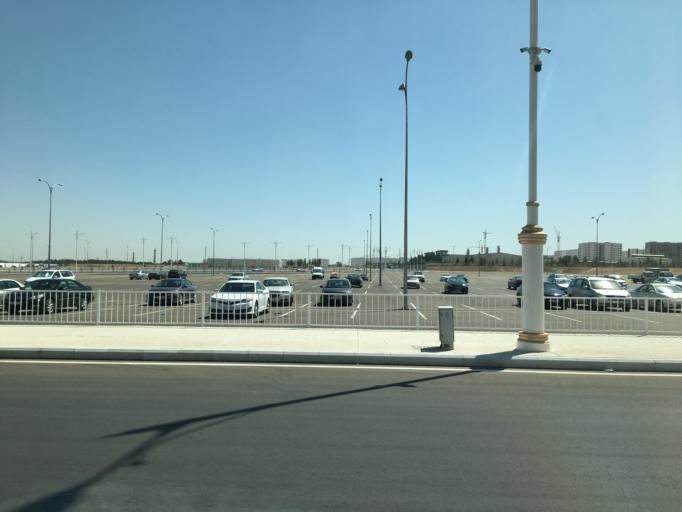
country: TM
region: Ahal
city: Ashgabat
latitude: 37.9010
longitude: 58.3977
